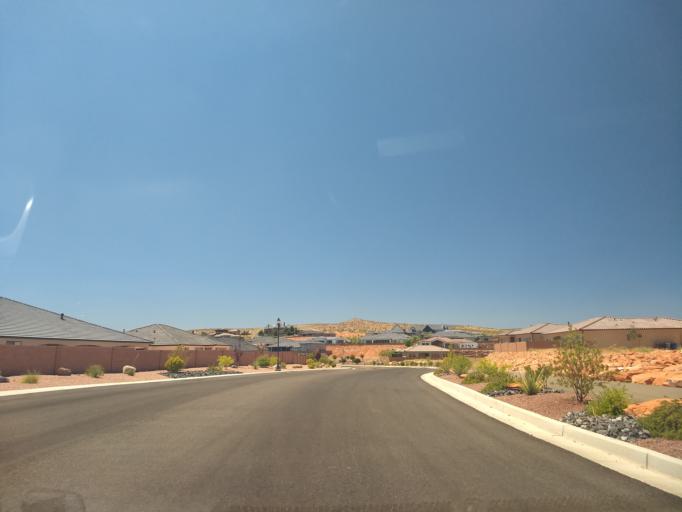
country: US
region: Utah
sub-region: Washington County
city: Washington
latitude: 37.1582
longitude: -113.5300
